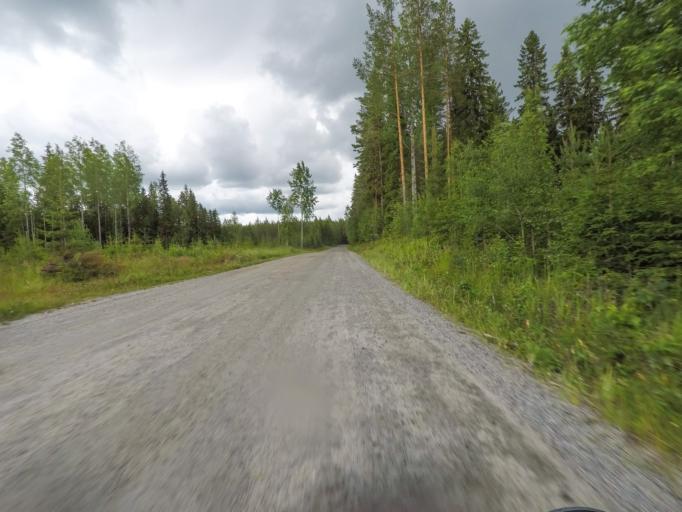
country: FI
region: Central Finland
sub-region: Jyvaeskylae
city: Hankasalmi
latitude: 62.3944
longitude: 26.5977
